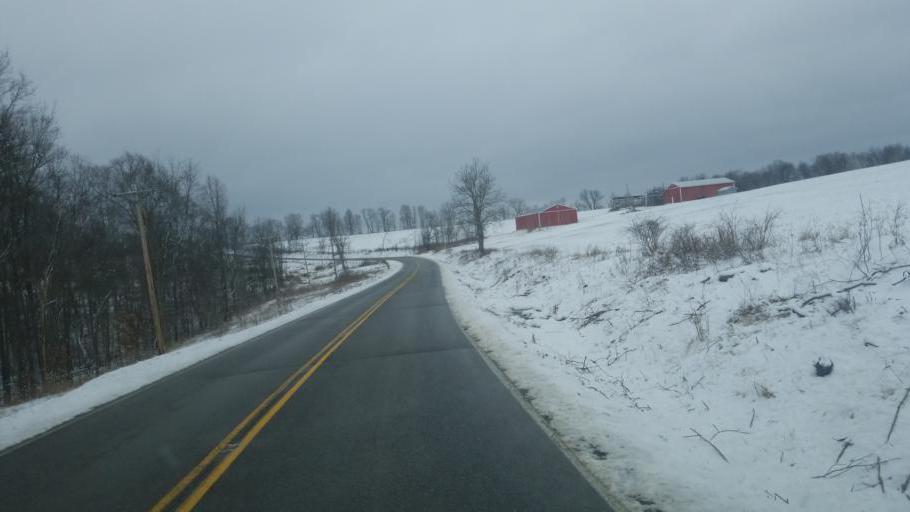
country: US
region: Ohio
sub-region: Knox County
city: Oak Hill
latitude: 40.4299
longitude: -82.1415
